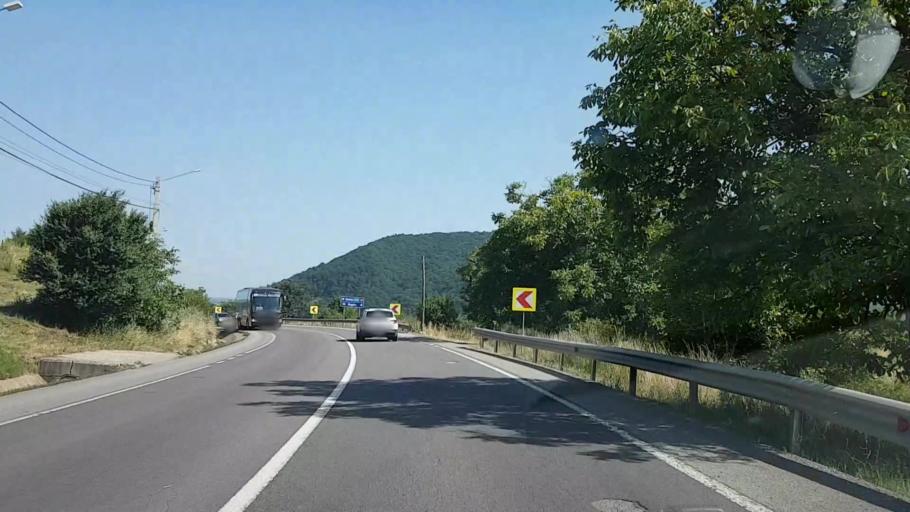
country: RO
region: Bistrita-Nasaud
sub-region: Comuna Sieu-Magherus
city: Sieu-Magherus
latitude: 47.0643
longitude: 24.4142
